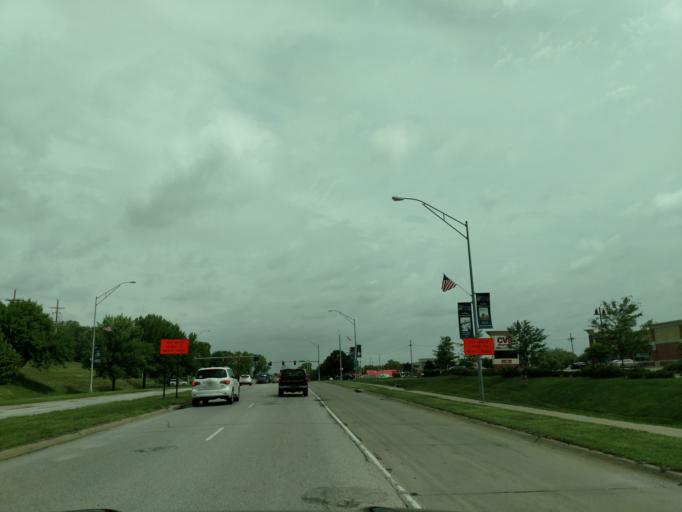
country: US
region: Nebraska
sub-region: Sarpy County
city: La Vista
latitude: 41.1893
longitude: -96.0431
